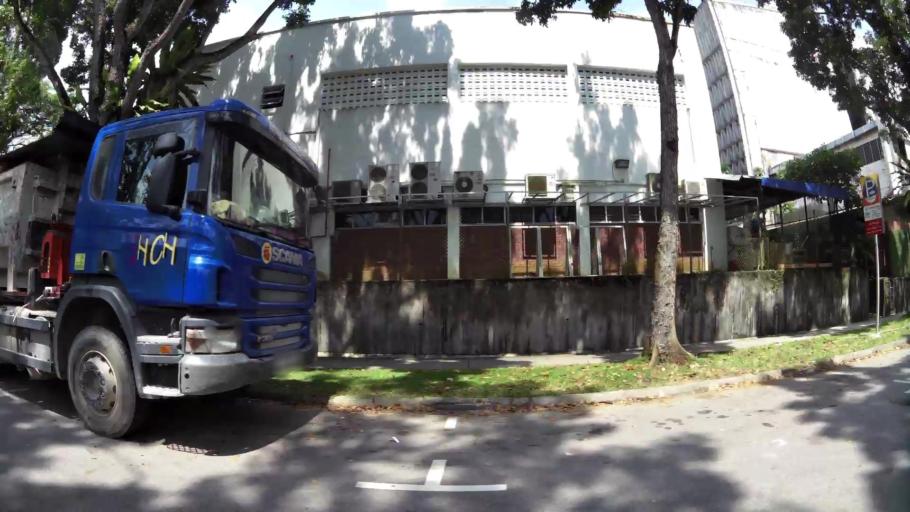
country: SG
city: Singapore
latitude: 1.3825
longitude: 103.8269
